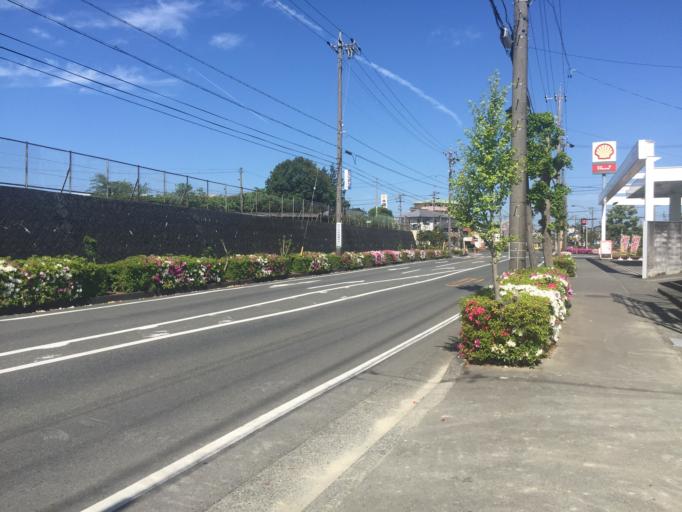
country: JP
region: Shizuoka
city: Kakegawa
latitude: 34.7656
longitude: 138.0103
